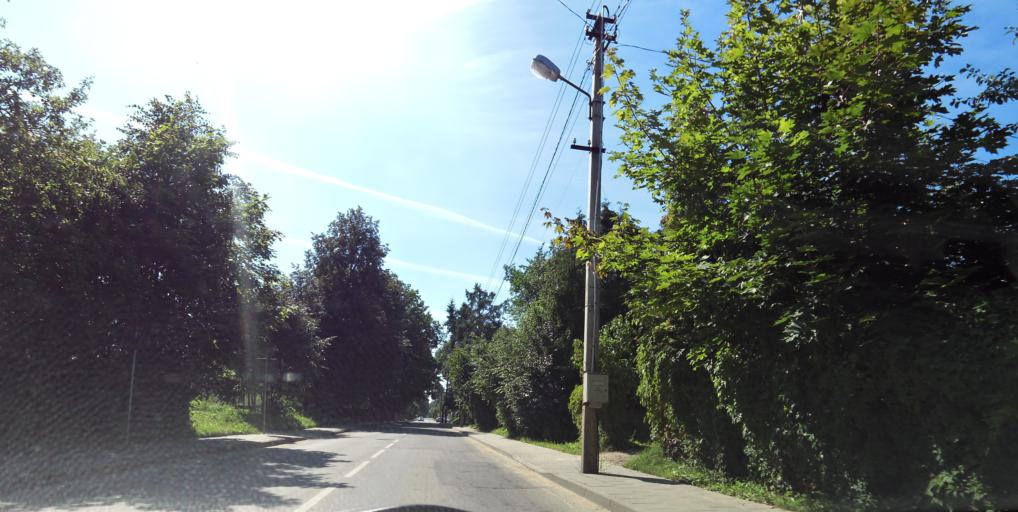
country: LT
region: Vilnius County
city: Rasos
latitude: 54.6721
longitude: 25.3619
